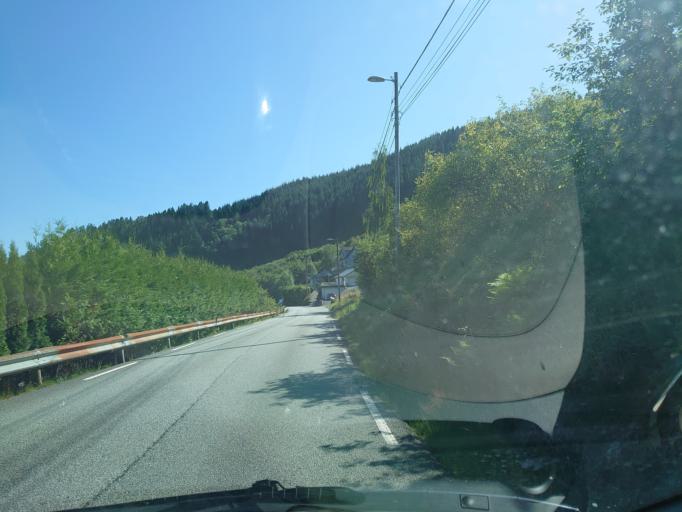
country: NO
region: Hordaland
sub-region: Bergen
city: Indre Arna
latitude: 60.4396
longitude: 5.4782
